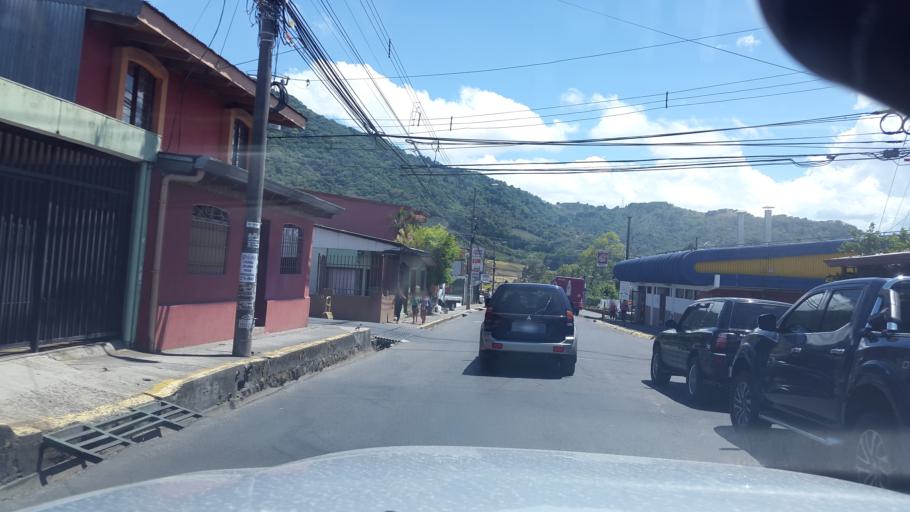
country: CR
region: Cartago
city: Tres Rios
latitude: 9.9063
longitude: -83.9880
